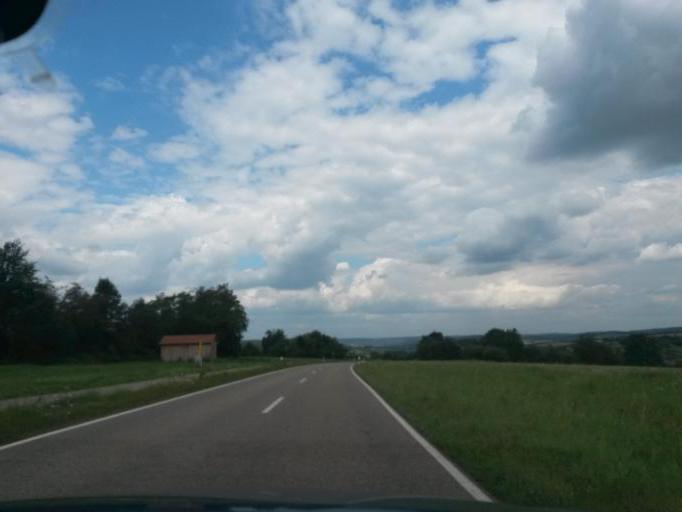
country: DE
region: Baden-Wuerttemberg
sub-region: Karlsruhe Region
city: Neuenburg
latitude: 48.8662
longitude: 8.5355
